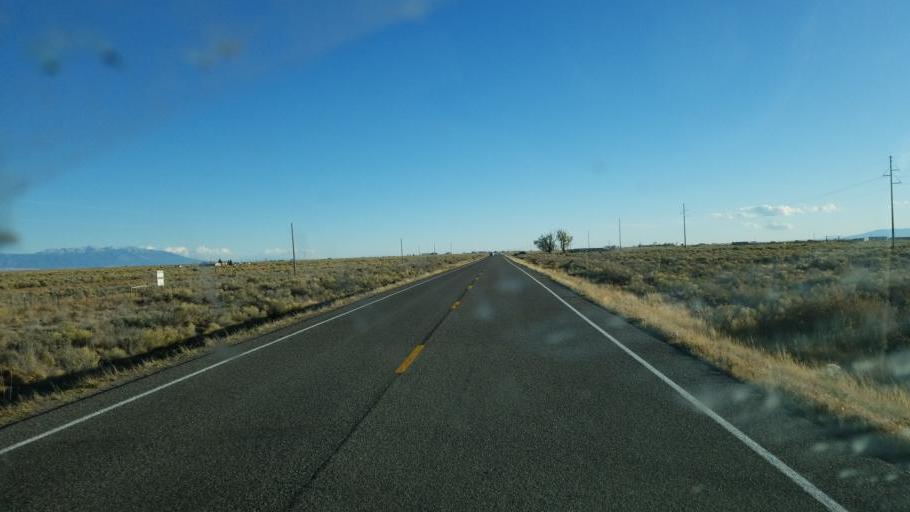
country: US
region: Colorado
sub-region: Saguache County
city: Saguache
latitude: 38.0900
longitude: -105.9186
